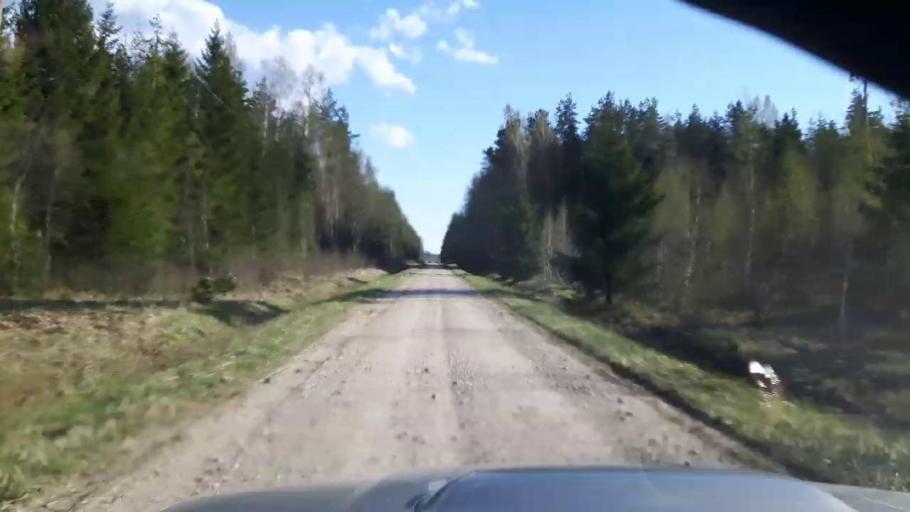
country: EE
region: Paernumaa
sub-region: Tootsi vald
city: Tootsi
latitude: 58.4254
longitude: 24.8515
